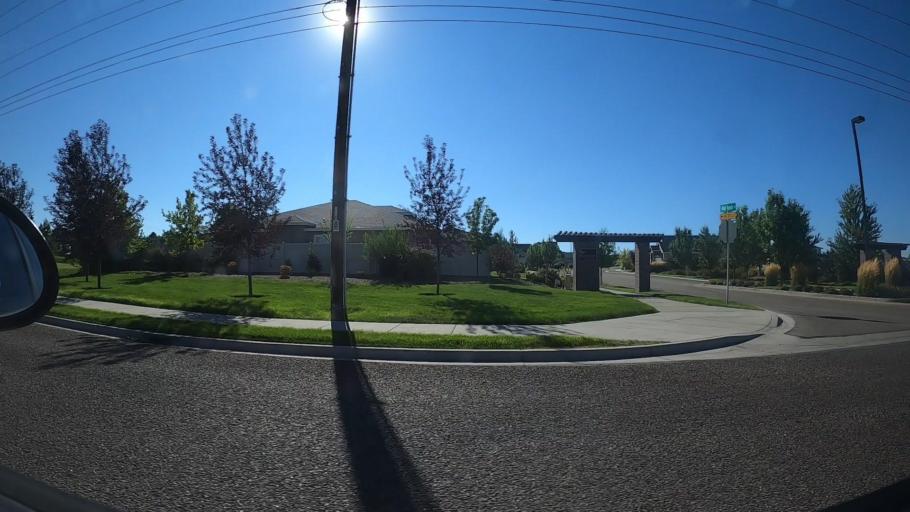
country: US
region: Idaho
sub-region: Canyon County
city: Nampa
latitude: 43.5517
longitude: -116.6127
